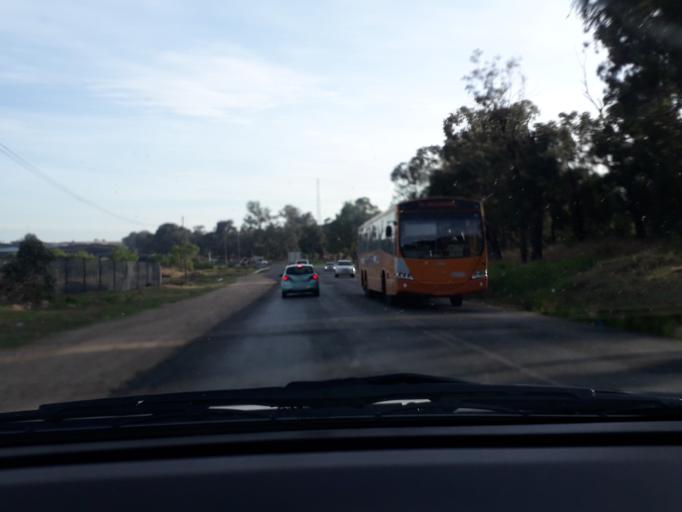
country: ZA
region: Gauteng
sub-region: City of Tshwane Metropolitan Municipality
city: Centurion
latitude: -25.9179
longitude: 28.1557
